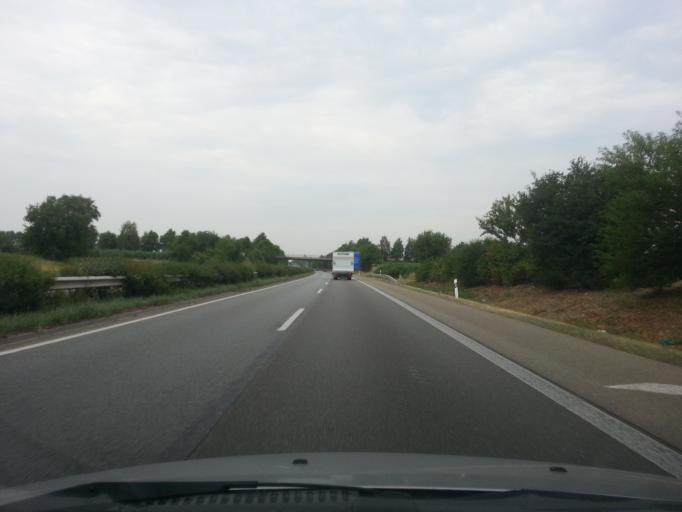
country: DE
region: Rheinland-Pfalz
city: Kirrweiler
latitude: 49.2981
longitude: 8.1522
